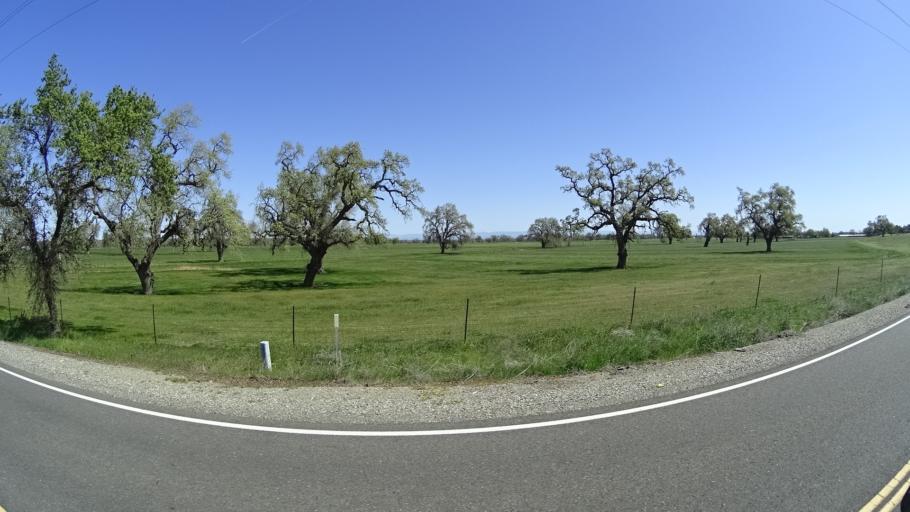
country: US
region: California
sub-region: Glenn County
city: Orland
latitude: 39.7924
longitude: -122.3119
